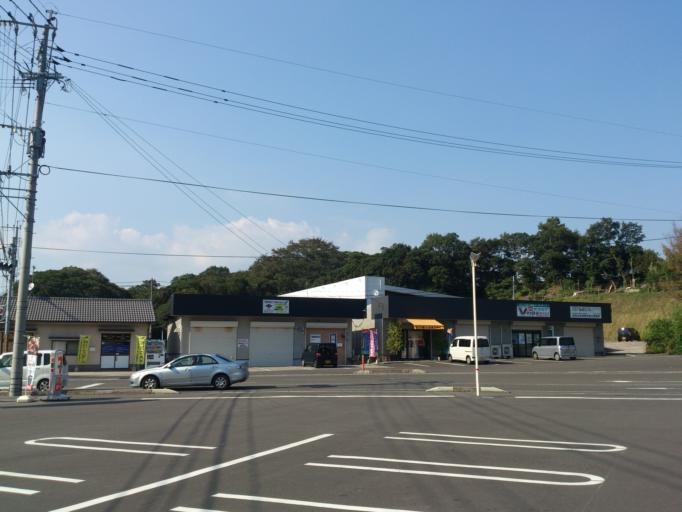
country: JP
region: Kagoshima
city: Kanoya
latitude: 31.3671
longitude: 130.8621
